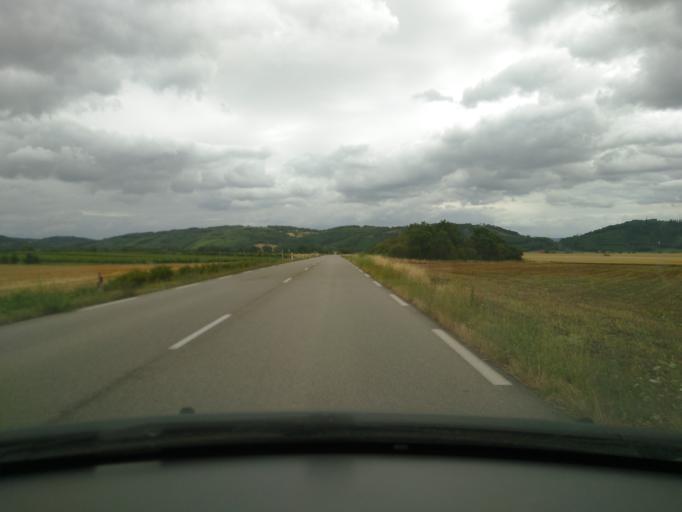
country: FR
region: Rhone-Alpes
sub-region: Departement de l'Isere
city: La Cote-Saint-Andre
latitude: 45.4247
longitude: 5.2188
